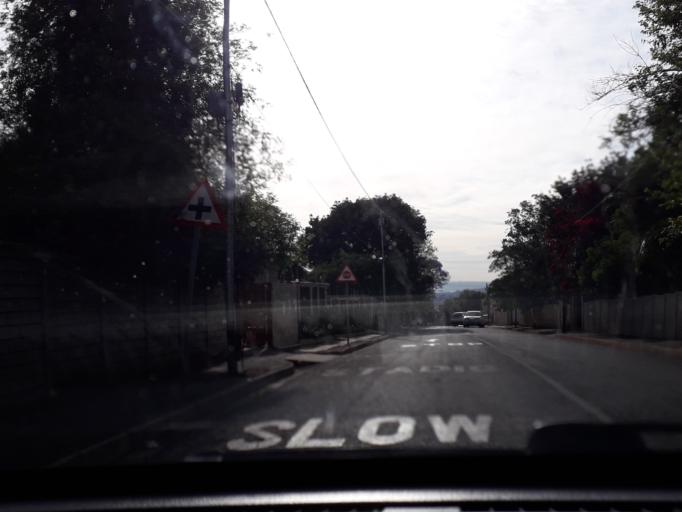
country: ZA
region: Gauteng
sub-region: City of Johannesburg Metropolitan Municipality
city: Johannesburg
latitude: -26.1571
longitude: 28.0906
